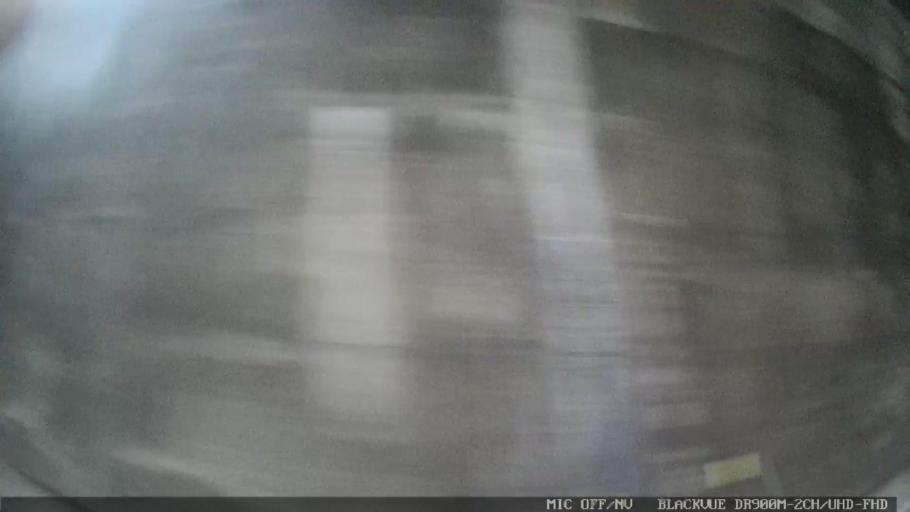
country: BR
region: Sao Paulo
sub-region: Cubatao
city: Cubatao
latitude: -23.8803
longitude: -46.4855
